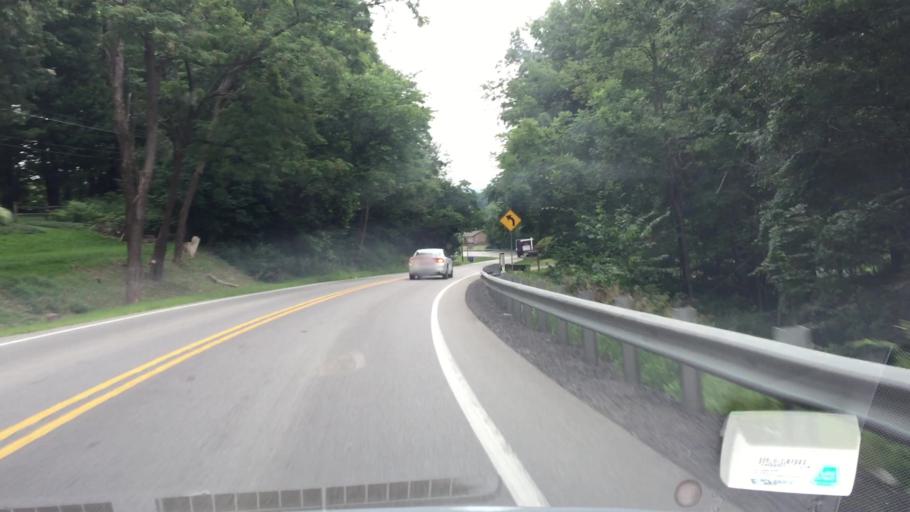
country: US
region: Pennsylvania
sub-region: Butler County
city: Saxonburg
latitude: 40.7239
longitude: -79.8756
